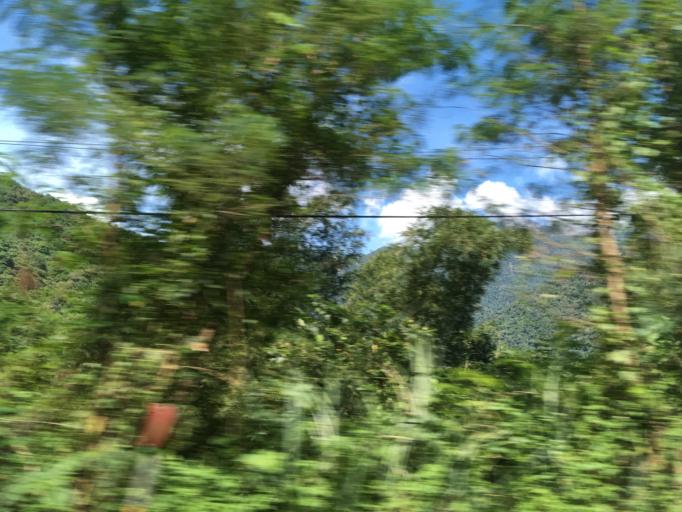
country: TW
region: Taiwan
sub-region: Yilan
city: Yilan
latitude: 24.4385
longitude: 121.7606
